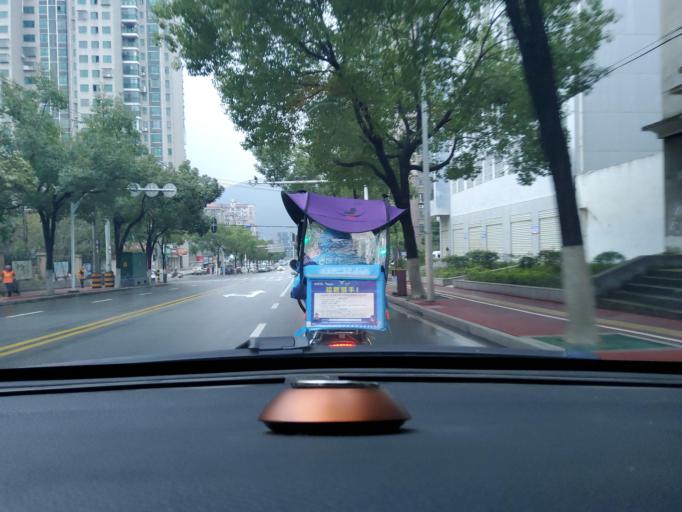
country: CN
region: Hubei
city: Tuanchengshan
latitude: 30.1900
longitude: 115.0274
